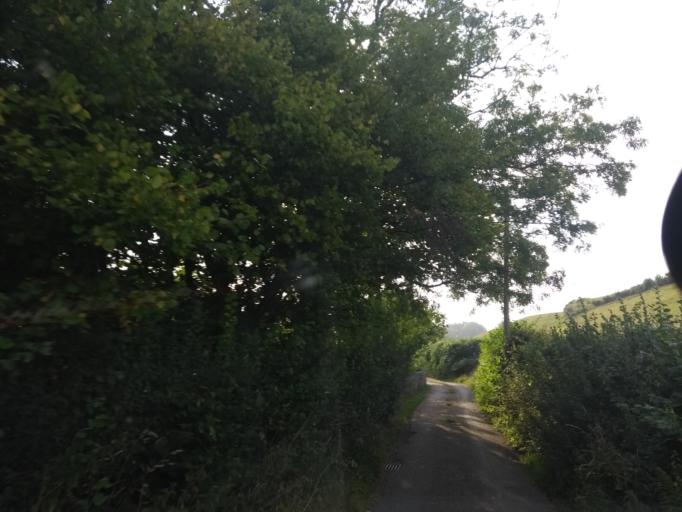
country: GB
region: England
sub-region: Devon
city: Colyton
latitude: 50.7972
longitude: -3.0870
